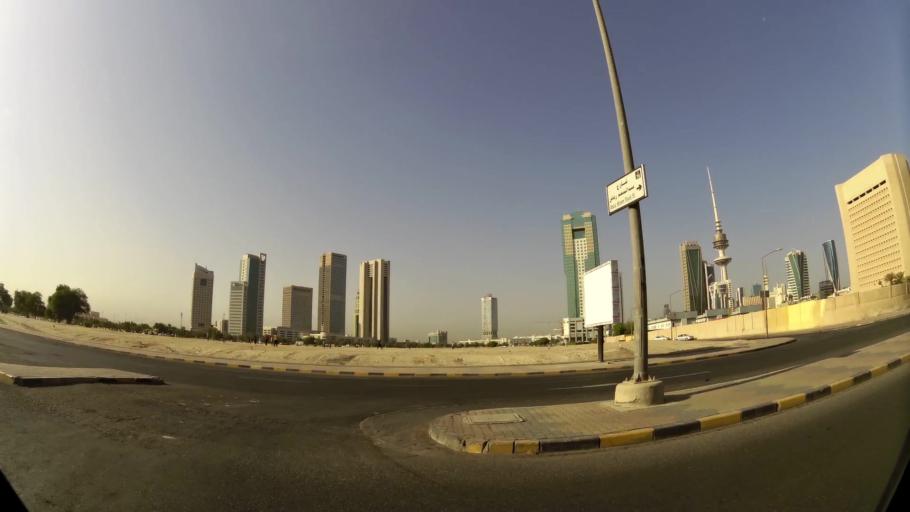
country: KW
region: Al Asimah
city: Kuwait City
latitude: 29.3702
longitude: 47.9851
